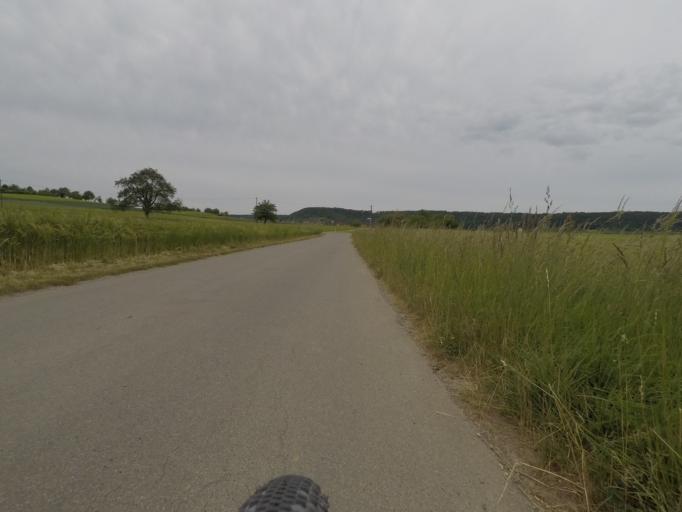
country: DE
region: Baden-Wuerttemberg
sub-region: Regierungsbezirk Stuttgart
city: Hildrizhausen
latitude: 48.5654
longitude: 8.9616
